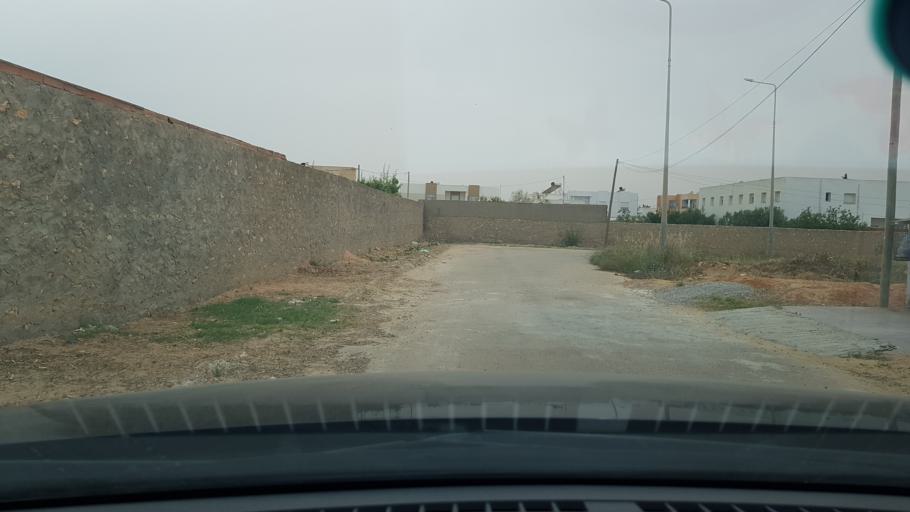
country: TN
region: Safaqis
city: Al Qarmadah
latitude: 34.8243
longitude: 10.7570
